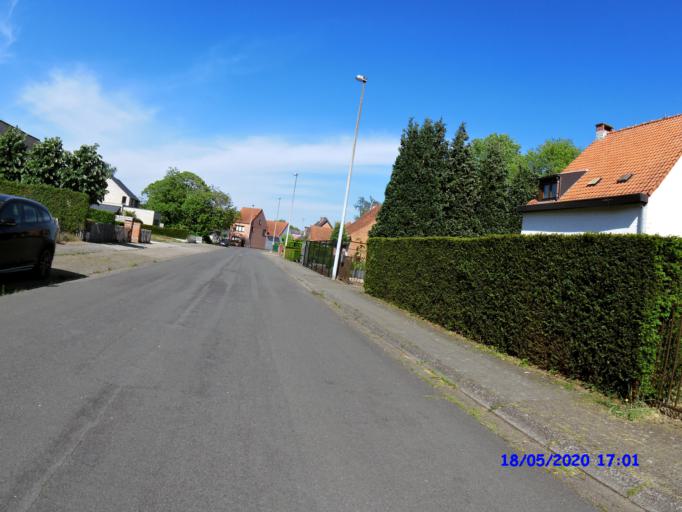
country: BE
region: Flanders
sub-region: Provincie Antwerpen
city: Herentals
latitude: 51.1813
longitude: 4.8220
